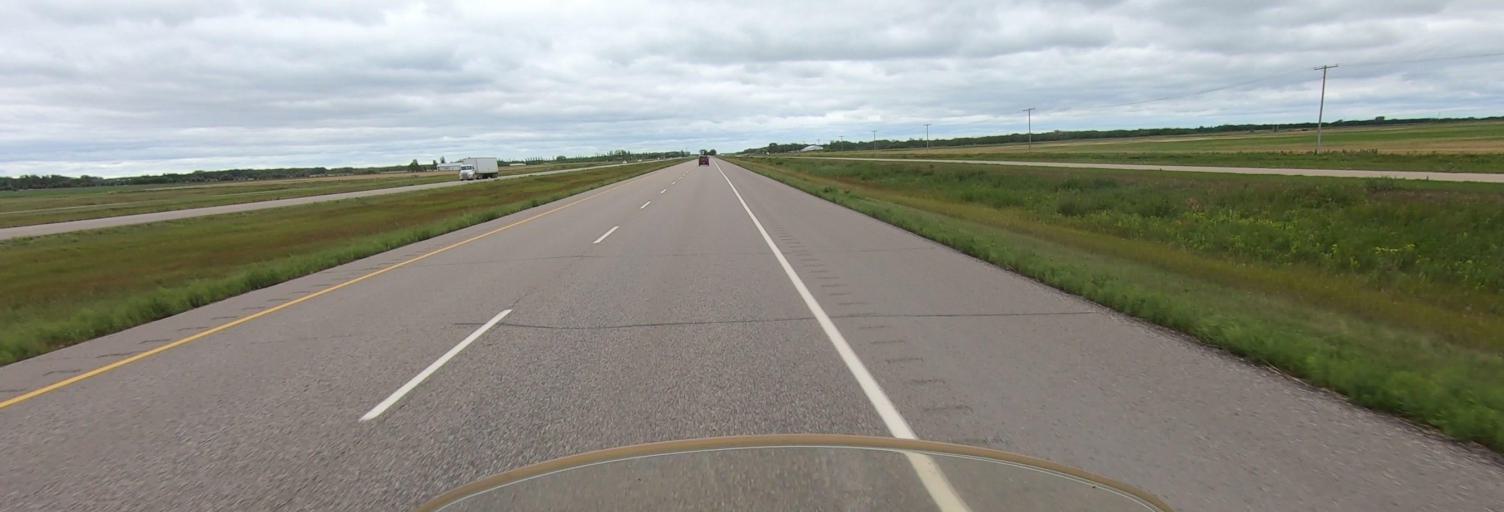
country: CA
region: Manitoba
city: Portage la Prairie
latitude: 49.9752
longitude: -98.6406
